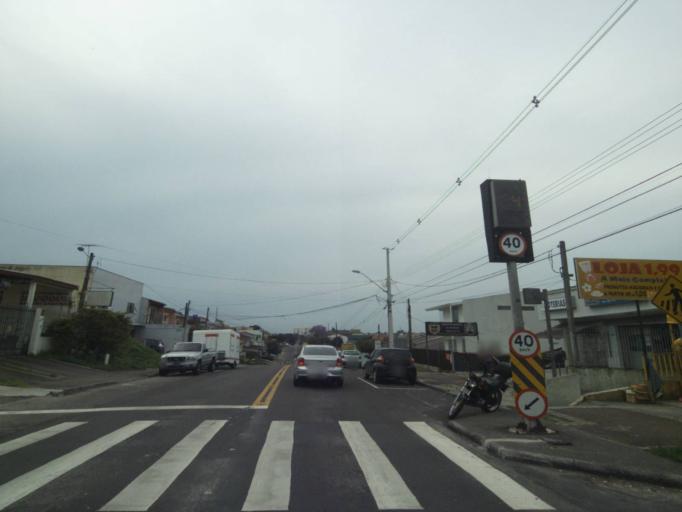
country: BR
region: Parana
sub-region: Pinhais
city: Pinhais
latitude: -25.4095
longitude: -49.2077
